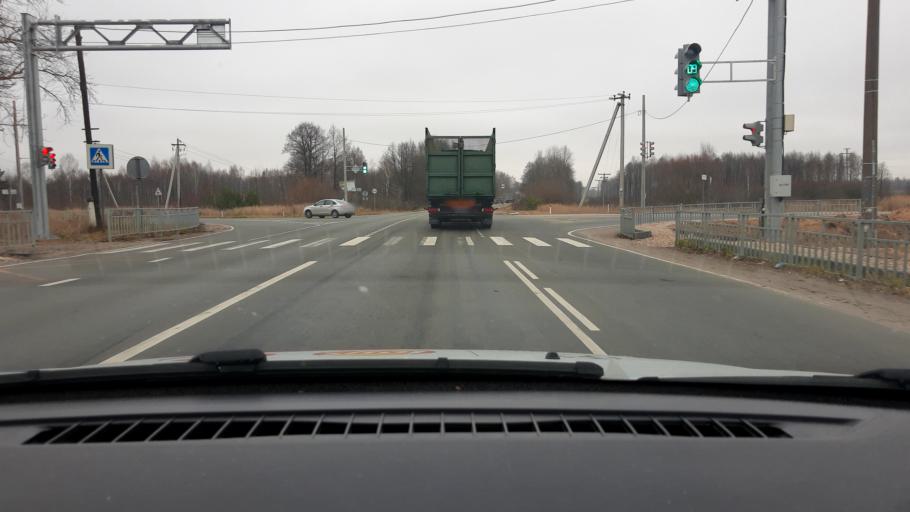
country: RU
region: Nizjnij Novgorod
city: Gorodets
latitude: 56.5682
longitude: 43.4830
